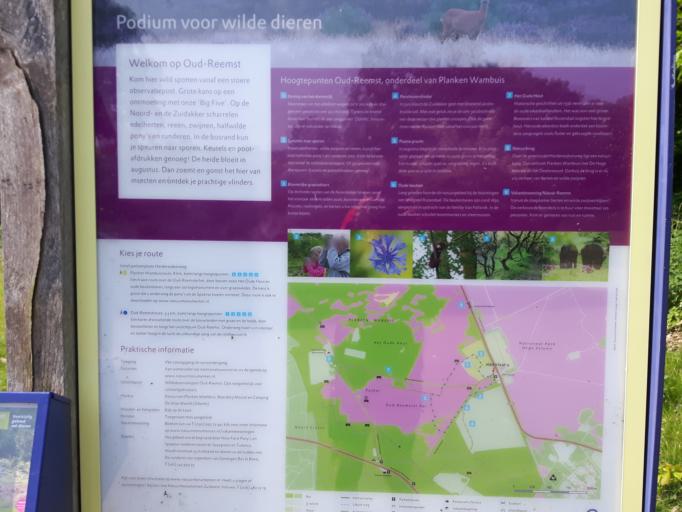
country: NL
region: Gelderland
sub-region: Gemeente Renkum
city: Wolfheze
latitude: 52.0432
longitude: 5.8085
